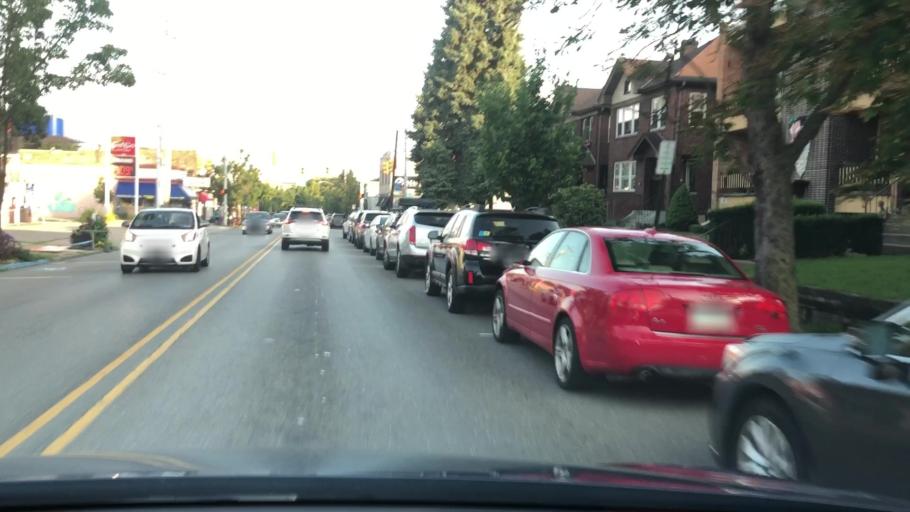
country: US
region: Pennsylvania
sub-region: Allegheny County
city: Edgewood
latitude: 40.4334
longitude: -79.8945
